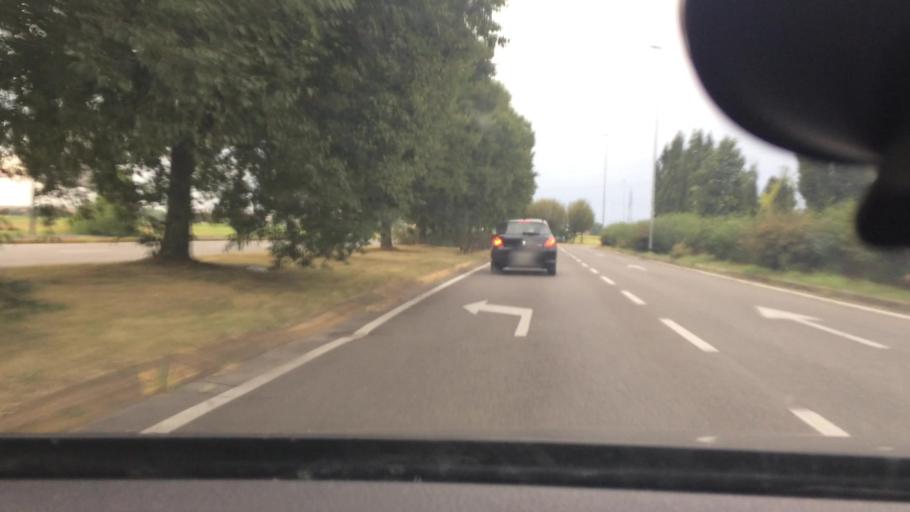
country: IT
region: Lombardy
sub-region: Citta metropolitana di Milano
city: Cusano Milanino
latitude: 45.5615
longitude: 9.1979
